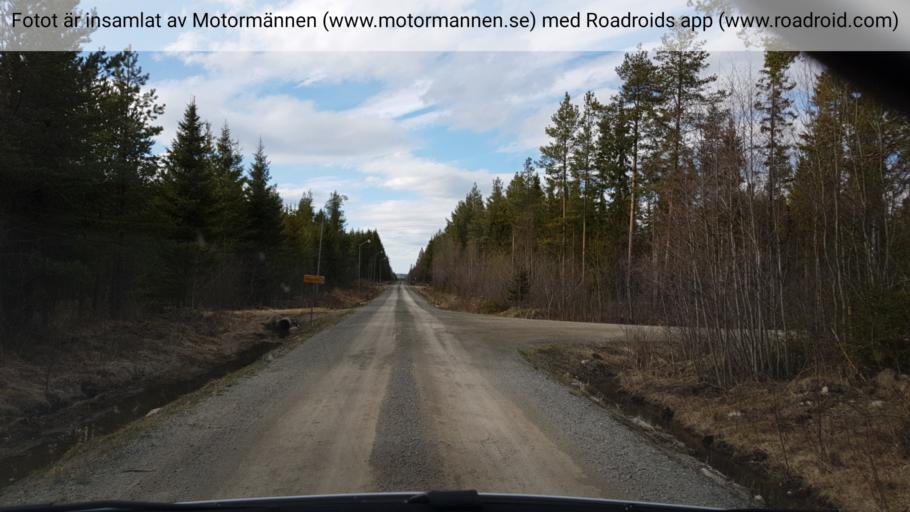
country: SE
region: Jaemtland
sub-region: Bergs Kommun
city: Hoverberg
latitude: 62.7985
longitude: 14.6742
